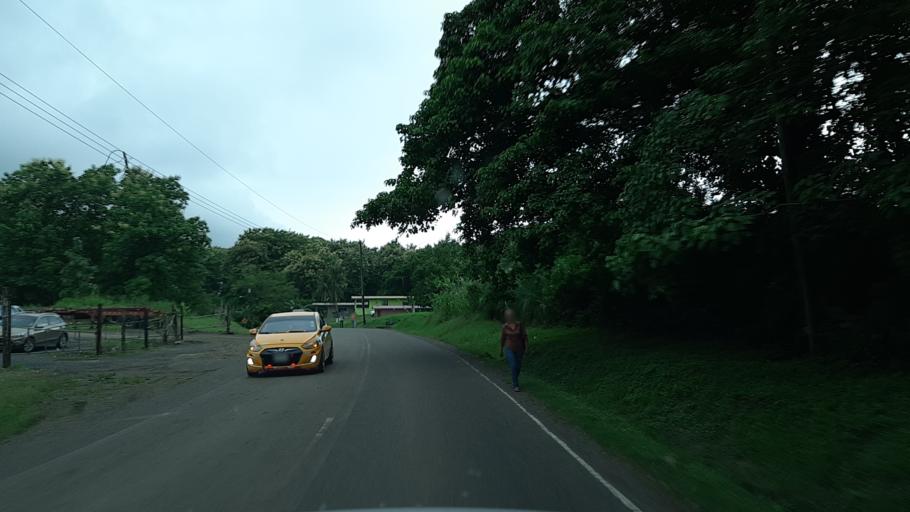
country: PA
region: Colon
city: Nuevo San Juan
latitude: 9.2454
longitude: -79.6570
